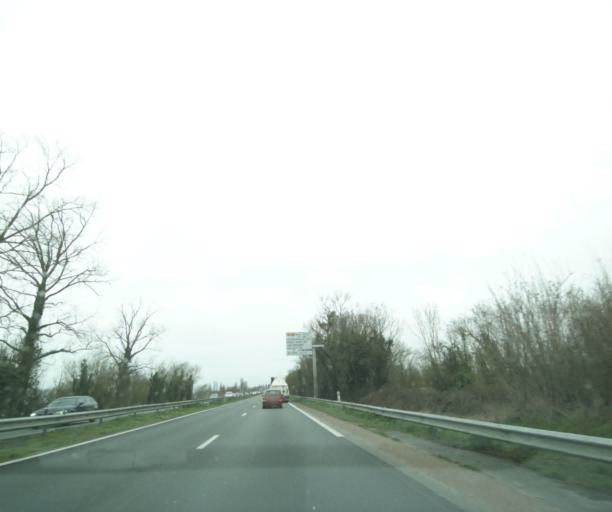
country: FR
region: Poitou-Charentes
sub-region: Departement de la Charente-Maritime
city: Angoulins
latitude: 46.1139
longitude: -1.1037
